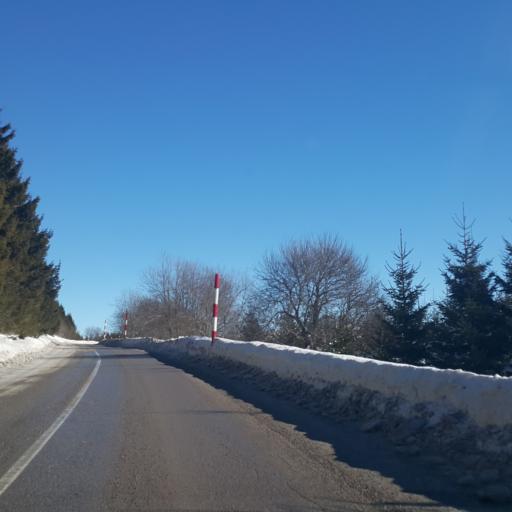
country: XK
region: Mitrovica
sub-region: Komuna e Leposaviqit
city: Leposaviq
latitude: 43.3251
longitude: 20.8488
